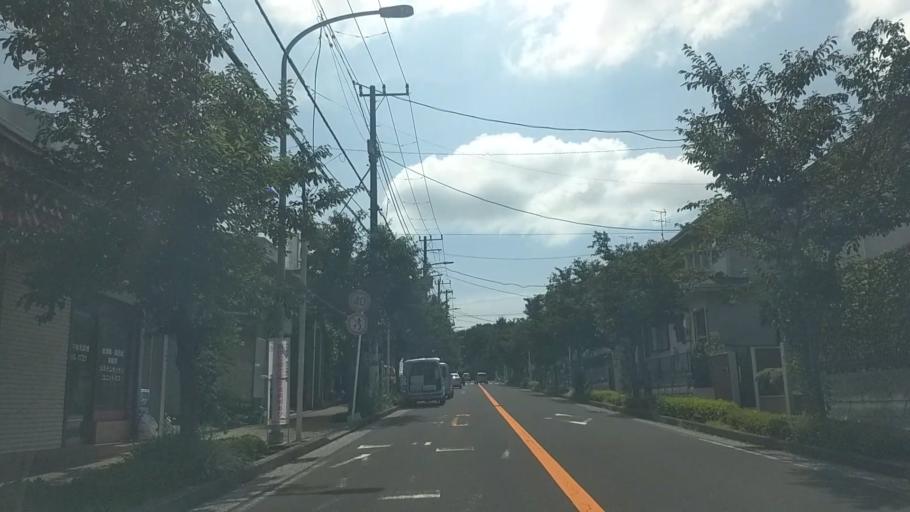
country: JP
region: Kanagawa
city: Zushi
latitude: 35.3478
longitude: 139.6278
